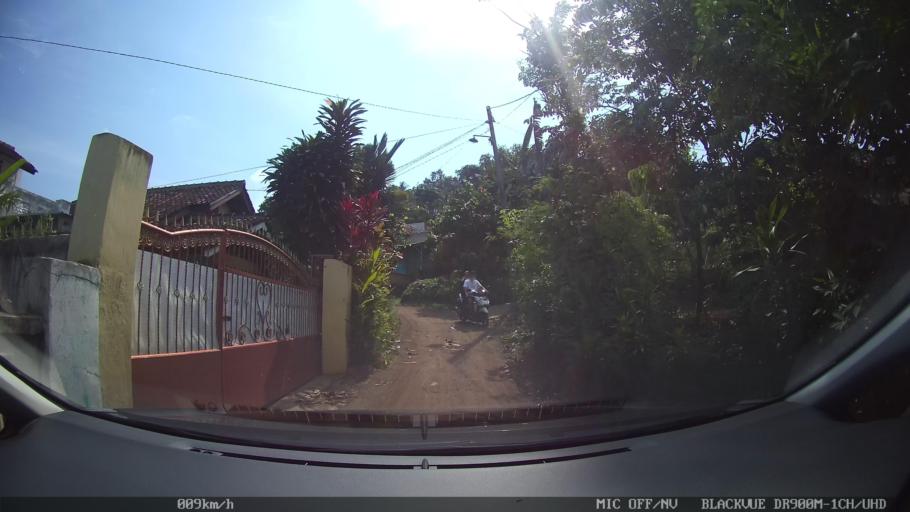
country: ID
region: Lampung
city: Kedaton
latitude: -5.3967
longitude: 105.2284
